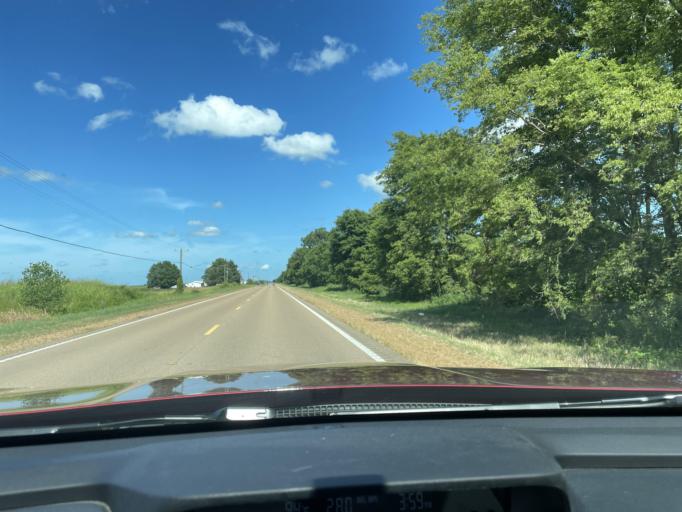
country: US
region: Mississippi
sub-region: Humphreys County
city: Belzoni
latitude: 33.1837
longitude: -90.5817
